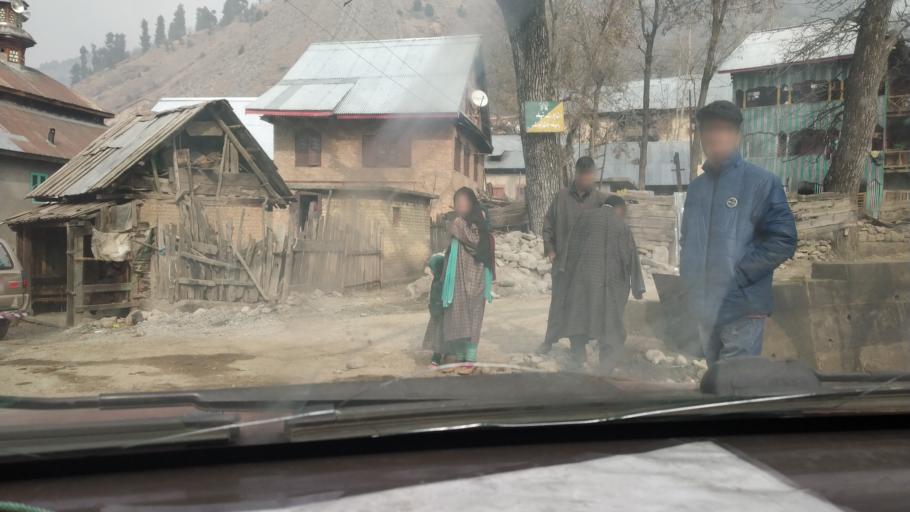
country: IN
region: Kashmir
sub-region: Ramban
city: Banihal
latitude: 33.4948
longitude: 75.3266
